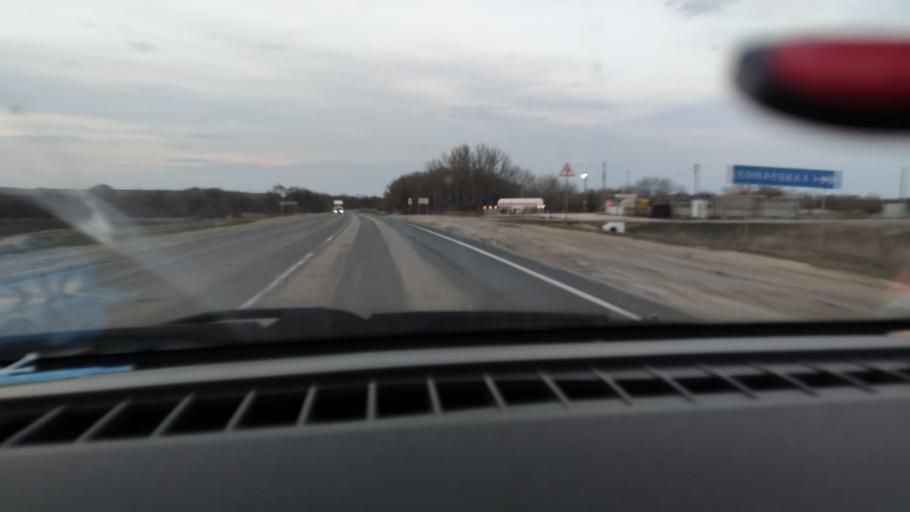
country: RU
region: Saratov
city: Sinodskoye
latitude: 51.9771
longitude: 46.6500
